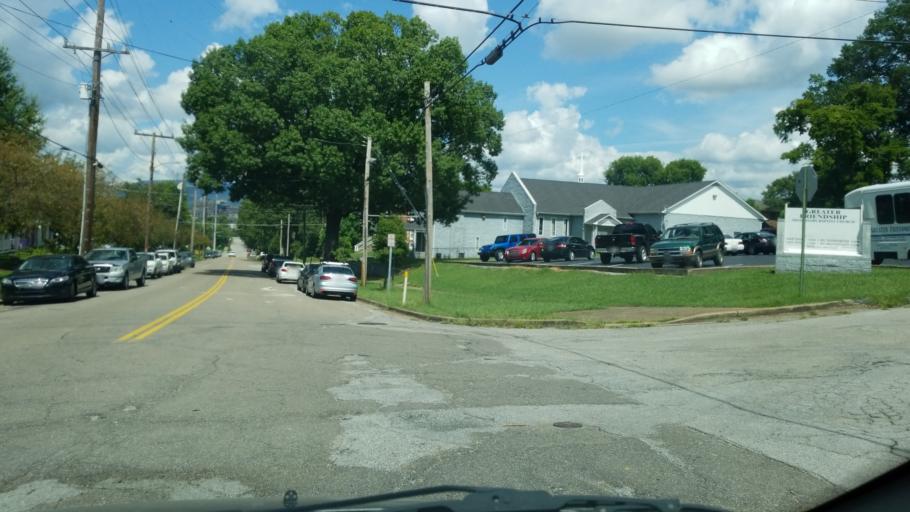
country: US
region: Tennessee
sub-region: Hamilton County
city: Chattanooga
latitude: 35.0393
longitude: -85.2943
